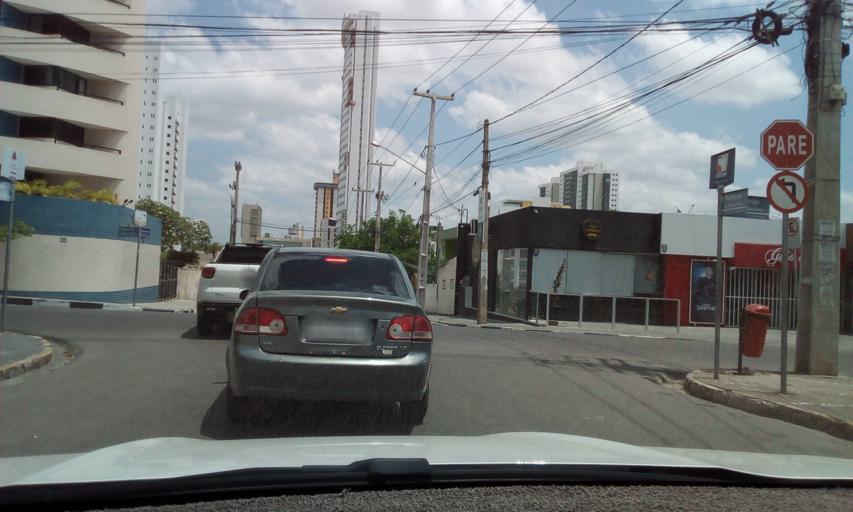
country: BR
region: Pernambuco
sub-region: Caruaru
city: Caruaru
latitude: -8.2704
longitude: -35.9749
